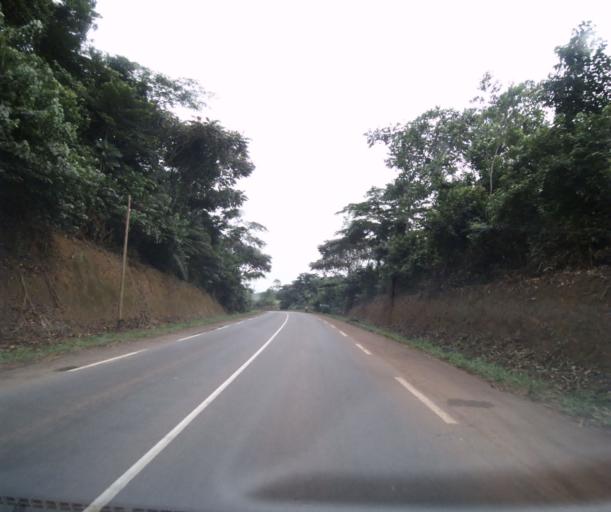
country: CM
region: Centre
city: Mbankomo
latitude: 3.7728
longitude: 11.1438
